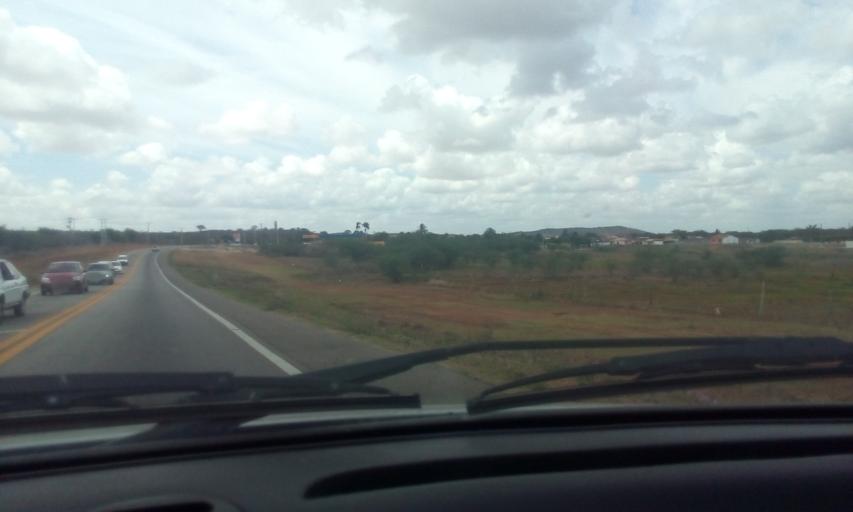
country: BR
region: Rio Grande do Norte
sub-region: Tangara
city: Tangara
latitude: -6.1087
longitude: -35.7101
